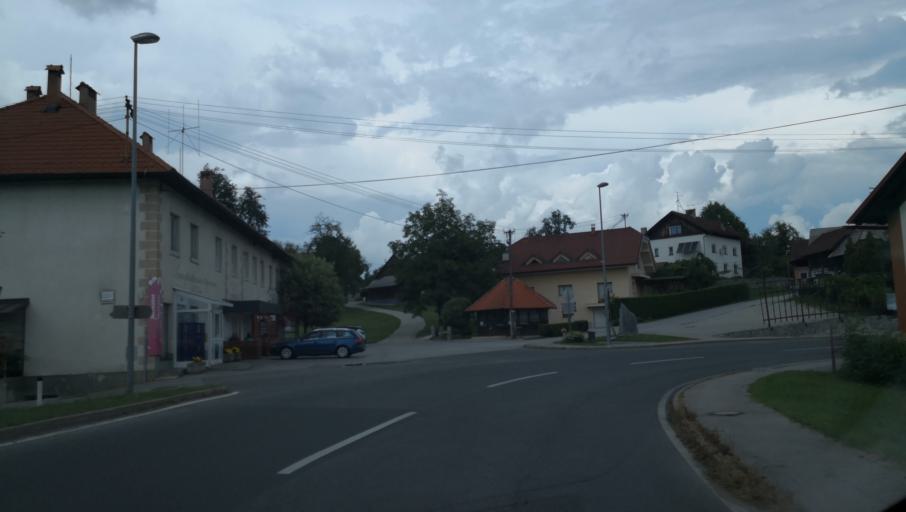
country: SI
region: Ivancna Gorica
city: Ivancna Gorica
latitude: 45.9016
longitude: 14.7987
